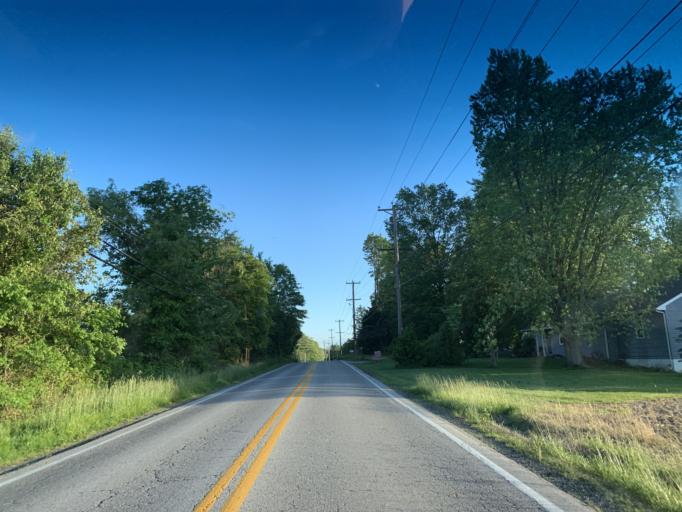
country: US
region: Maryland
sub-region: Cecil County
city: Elkton
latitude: 39.6364
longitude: -75.8146
